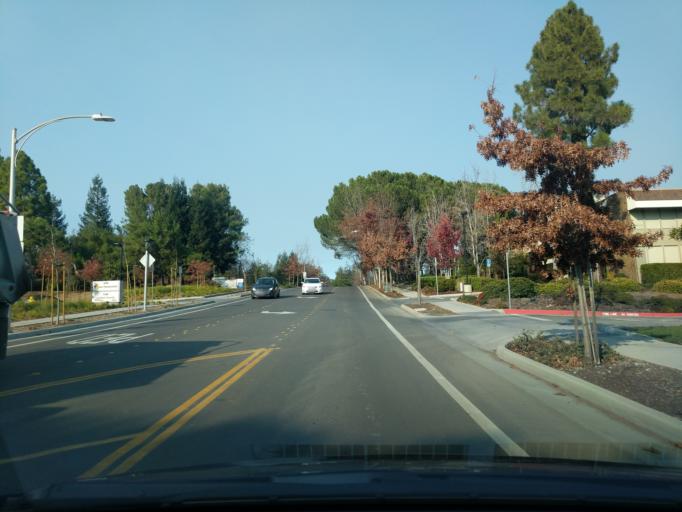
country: US
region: California
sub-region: Santa Clara County
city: Stanford
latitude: 37.4082
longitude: -122.1506
